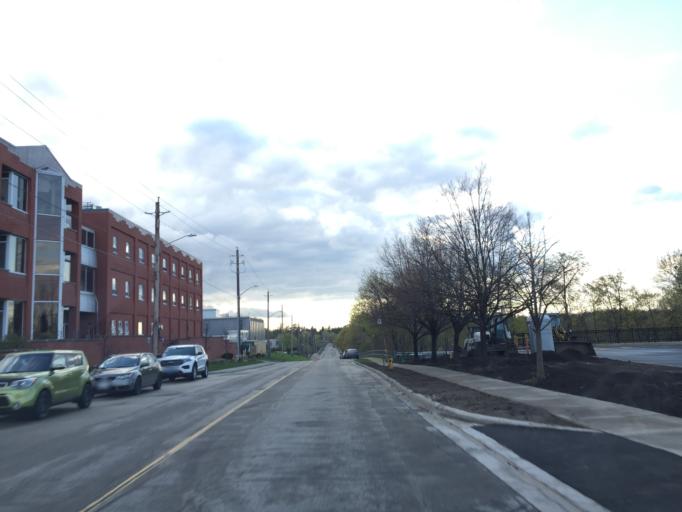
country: CA
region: Ontario
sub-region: Wellington County
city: Guelph
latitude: 43.5581
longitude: -80.2569
